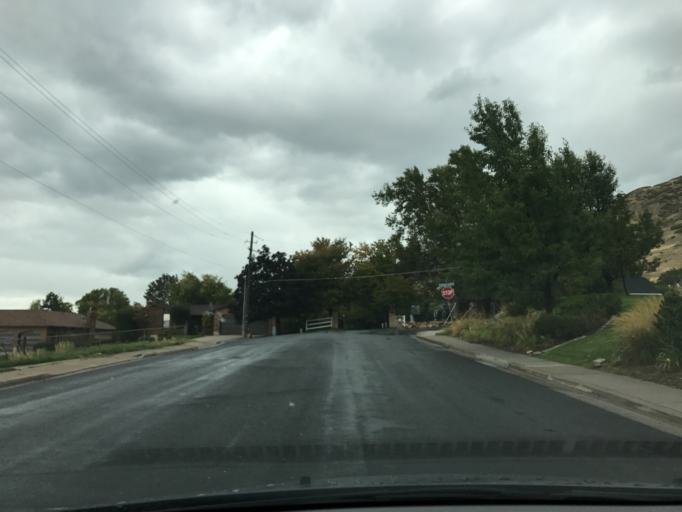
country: US
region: Utah
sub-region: Davis County
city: Farmington
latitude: 40.9979
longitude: -111.8942
